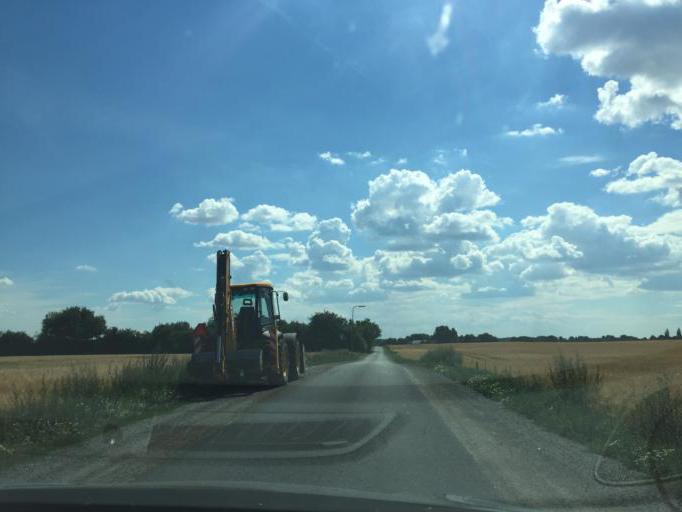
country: DK
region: South Denmark
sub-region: Odense Kommune
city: Bellinge
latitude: 55.3200
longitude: 10.3339
